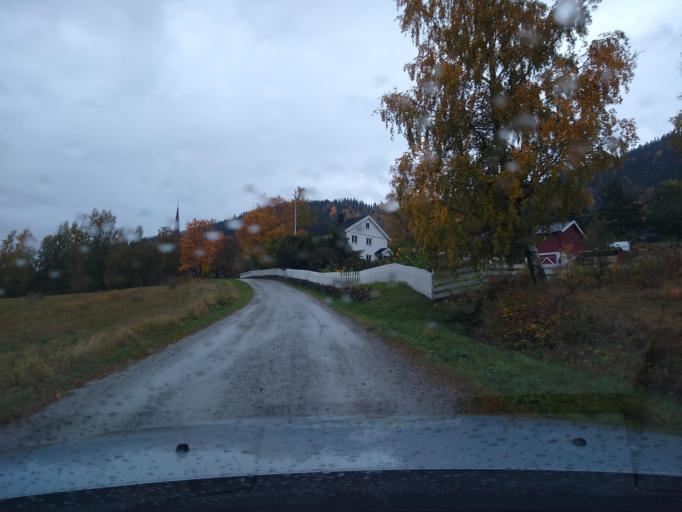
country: NO
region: Oppland
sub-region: Ringebu
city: Ringebu
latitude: 61.5072
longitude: 10.1727
